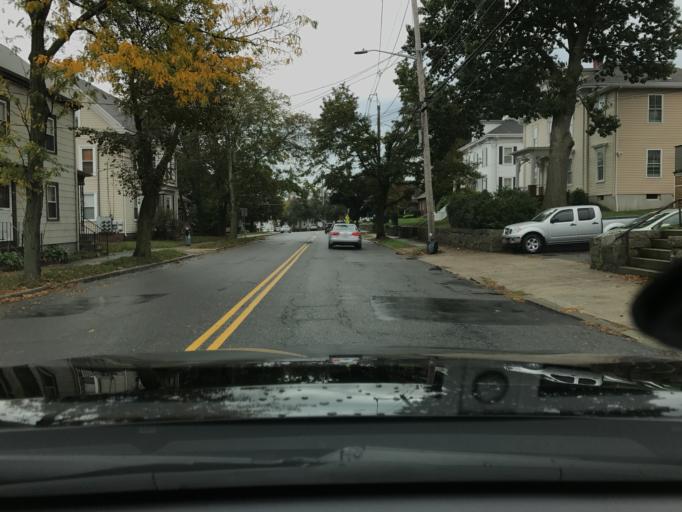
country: US
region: Massachusetts
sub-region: Essex County
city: Peabody
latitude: 42.5283
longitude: -70.9332
